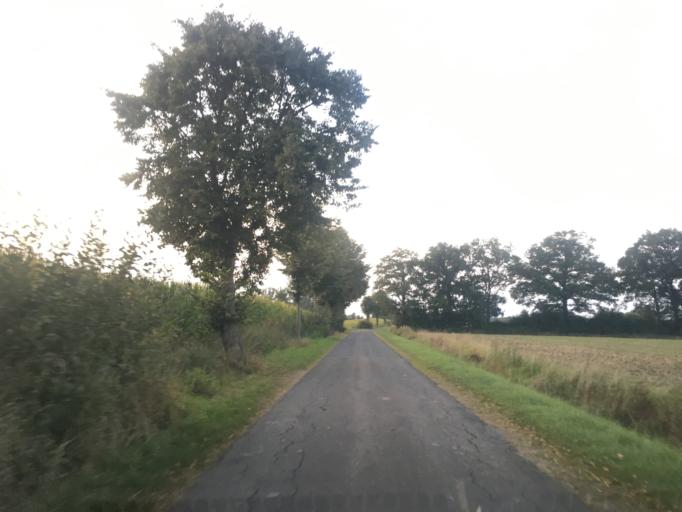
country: DE
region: North Rhine-Westphalia
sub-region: Regierungsbezirk Munster
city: Altenberge
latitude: 51.9997
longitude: 7.5260
